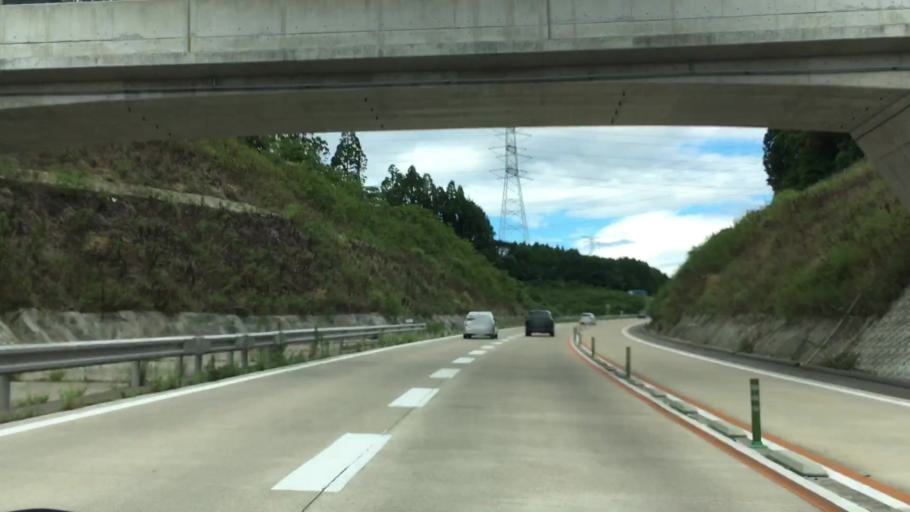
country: JP
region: Saga Prefecture
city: Imaricho-ko
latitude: 33.3514
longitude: 129.9245
